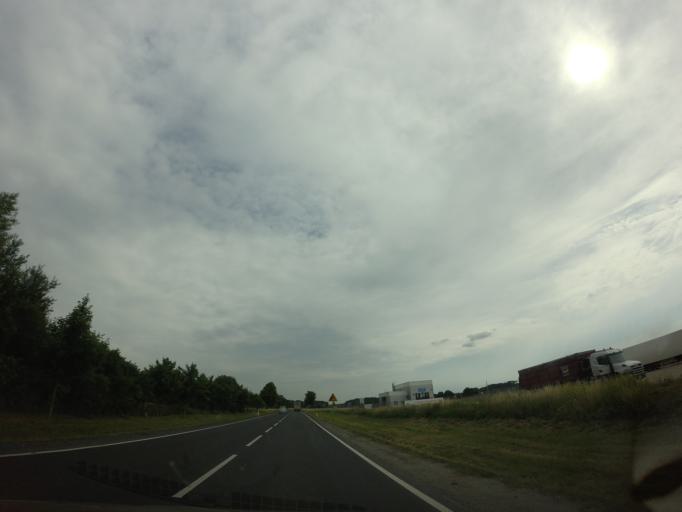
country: PL
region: West Pomeranian Voivodeship
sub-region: Powiat walecki
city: Miroslawiec
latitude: 53.3444
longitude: 16.0978
